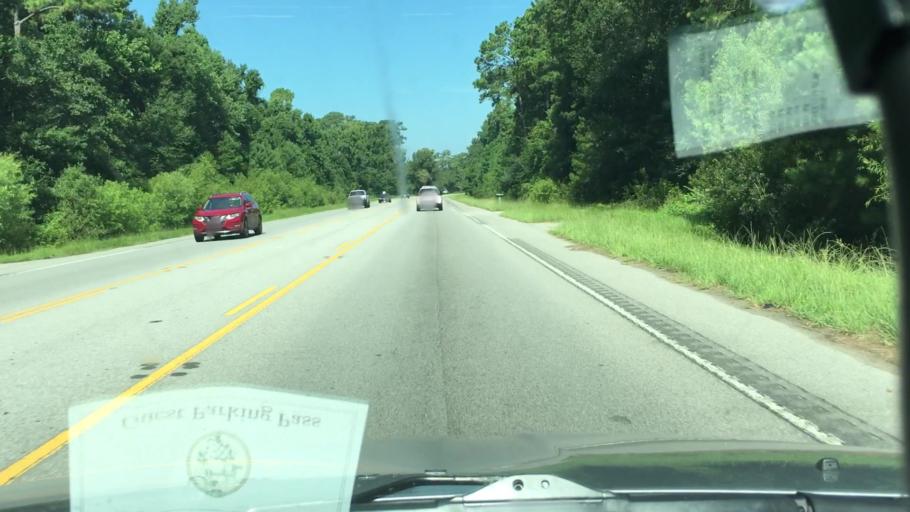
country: US
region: South Carolina
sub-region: Beaufort County
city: Beaufort
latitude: 32.3964
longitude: -80.5912
